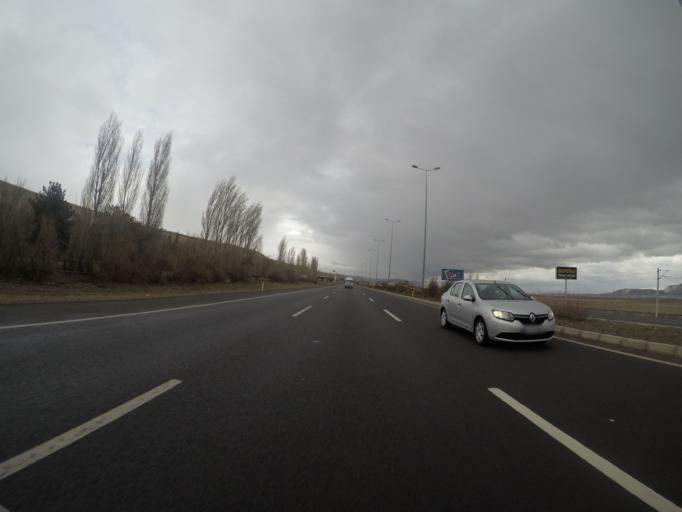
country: TR
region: Kayseri
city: Incesu
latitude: 38.7271
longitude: 35.2795
